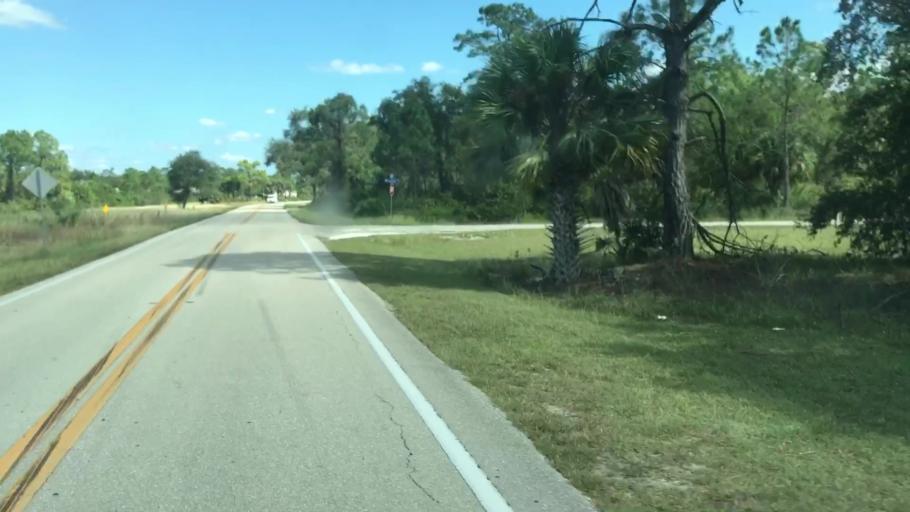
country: US
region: Florida
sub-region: Lee County
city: Lehigh Acres
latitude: 26.6422
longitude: -81.6599
